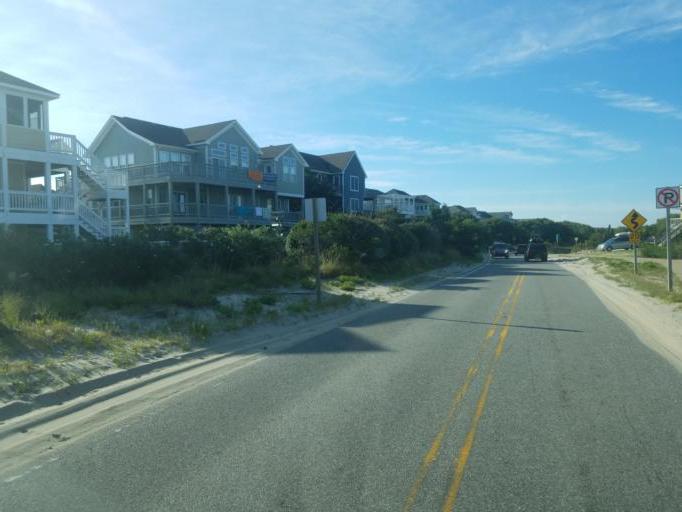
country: US
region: North Carolina
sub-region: Currituck County
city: Currituck
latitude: 36.3936
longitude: -75.8301
